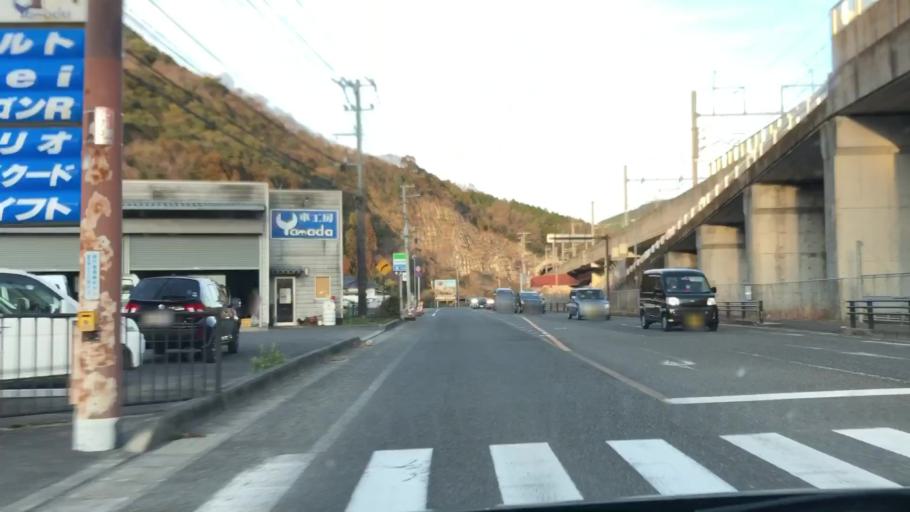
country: JP
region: Kumamoto
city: Minamata
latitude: 32.2127
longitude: 130.4310
